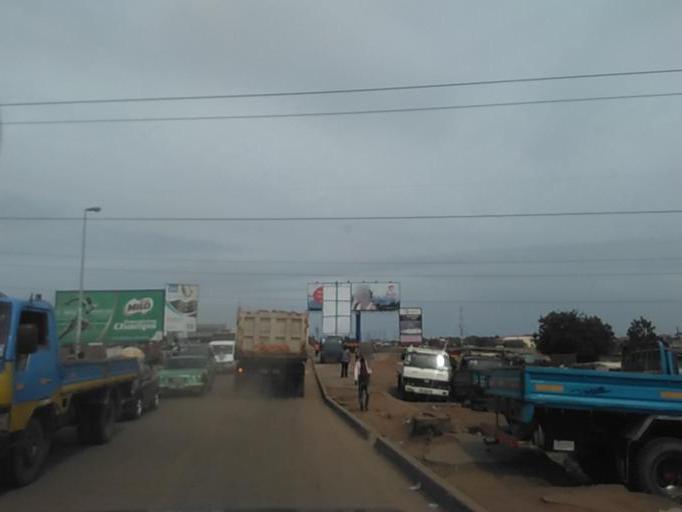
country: GH
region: Greater Accra
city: Tema
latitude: 5.6847
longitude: -0.0277
